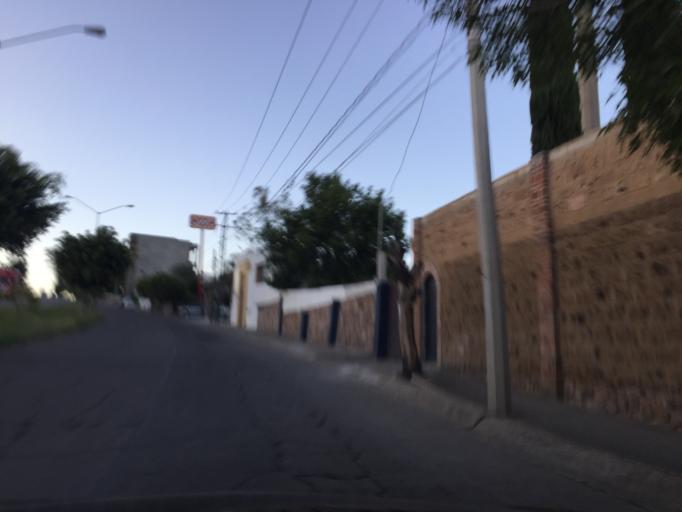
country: MX
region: Guanajuato
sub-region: Leon
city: La Ermita
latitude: 21.1606
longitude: -101.7076
